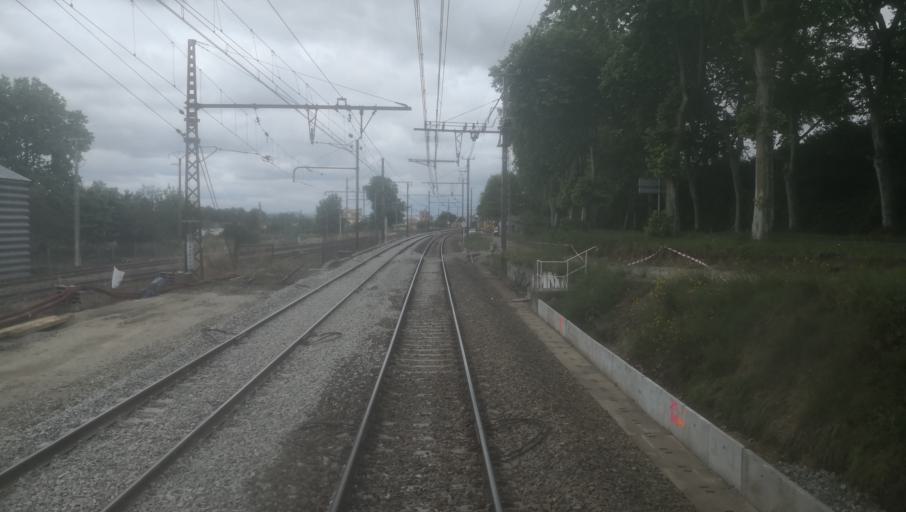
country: FR
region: Midi-Pyrenees
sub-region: Departement de la Haute-Garonne
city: Baziege
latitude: 43.4525
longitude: 1.6235
